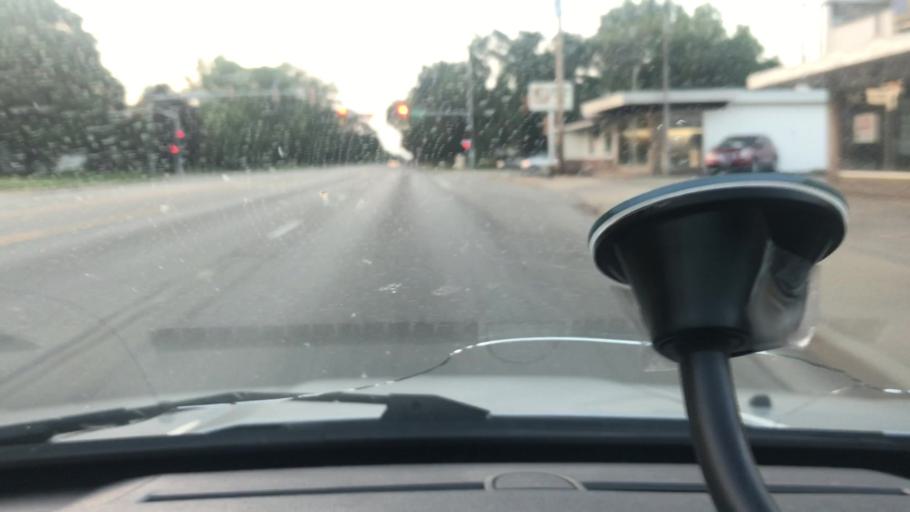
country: US
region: Illinois
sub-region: Tazewell County
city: Pekin
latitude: 40.5816
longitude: -89.6410
